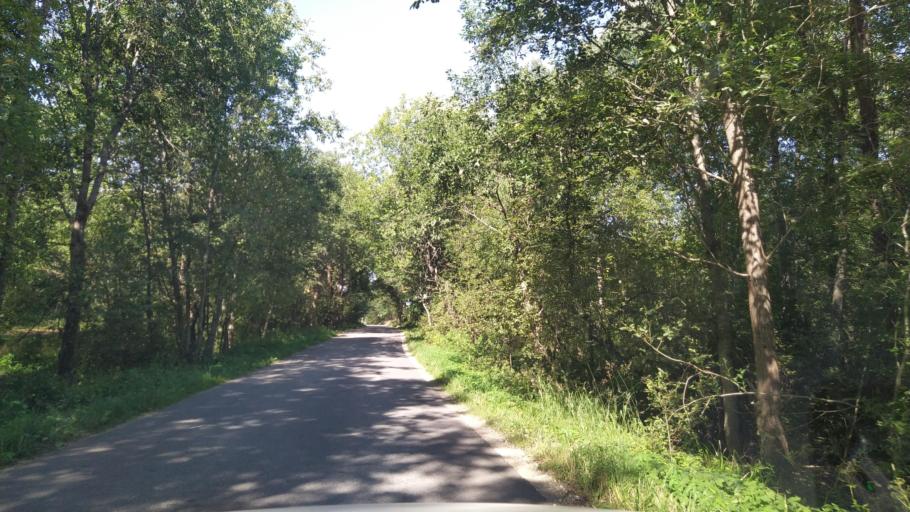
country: RU
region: Leningrad
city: Rozhdestveno
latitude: 59.2645
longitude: 30.0268
